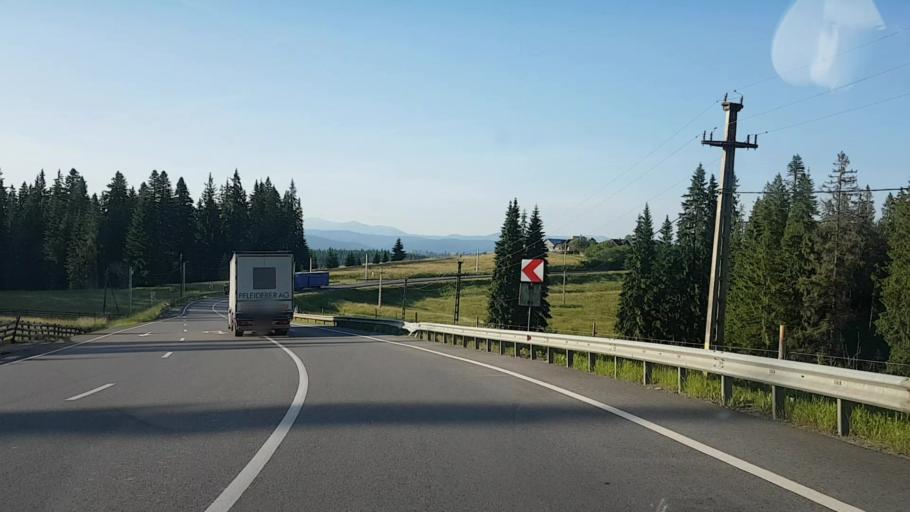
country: RO
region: Suceava
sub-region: Comuna Poiana Stampei
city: Poiana Stampei
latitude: 47.2898
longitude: 25.0770
